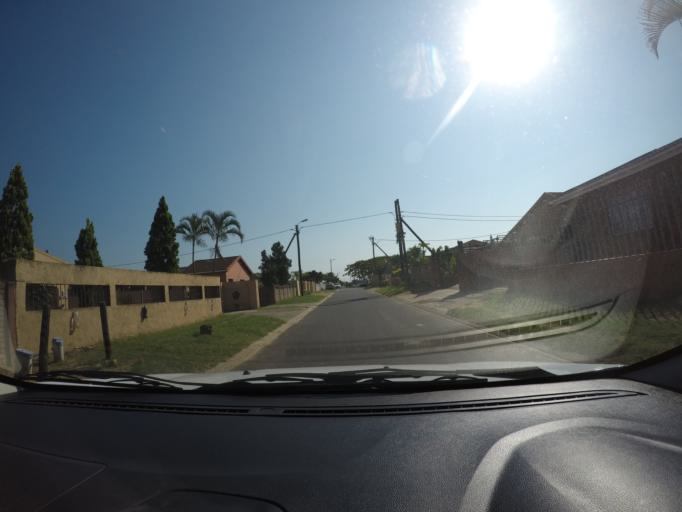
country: ZA
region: KwaZulu-Natal
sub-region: uThungulu District Municipality
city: Richards Bay
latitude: -28.7154
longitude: 32.0433
